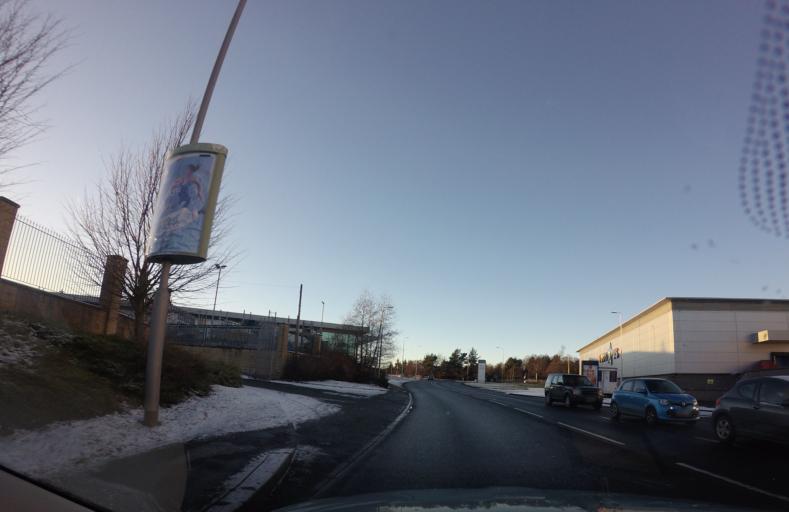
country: GB
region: Scotland
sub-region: Dundee City
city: Dundee
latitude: 56.4813
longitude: -2.9983
